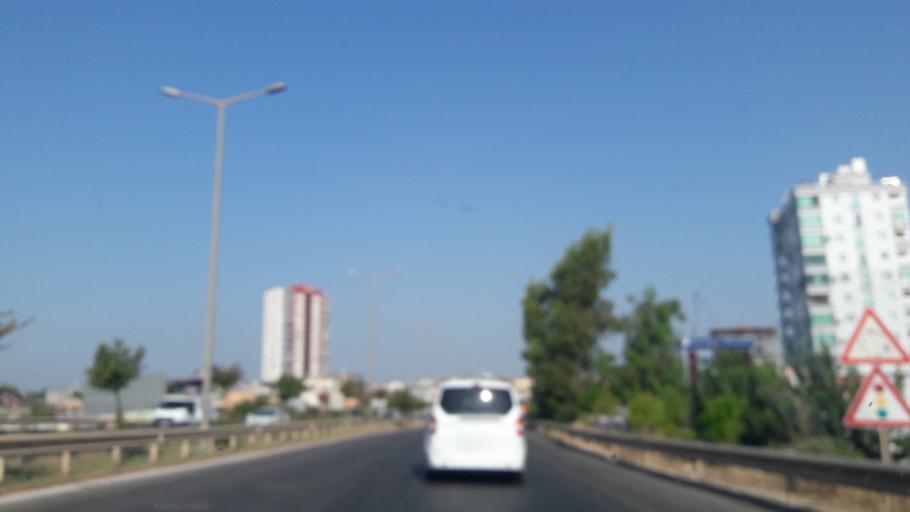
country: TR
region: Adana
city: Yuregir
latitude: 37.0234
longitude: 35.4013
